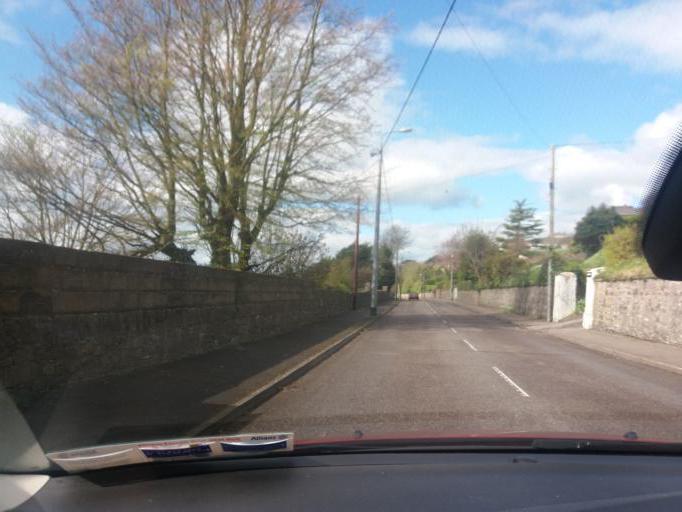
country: IE
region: Munster
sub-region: County Cork
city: Cobh
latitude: 51.8479
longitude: -8.3083
